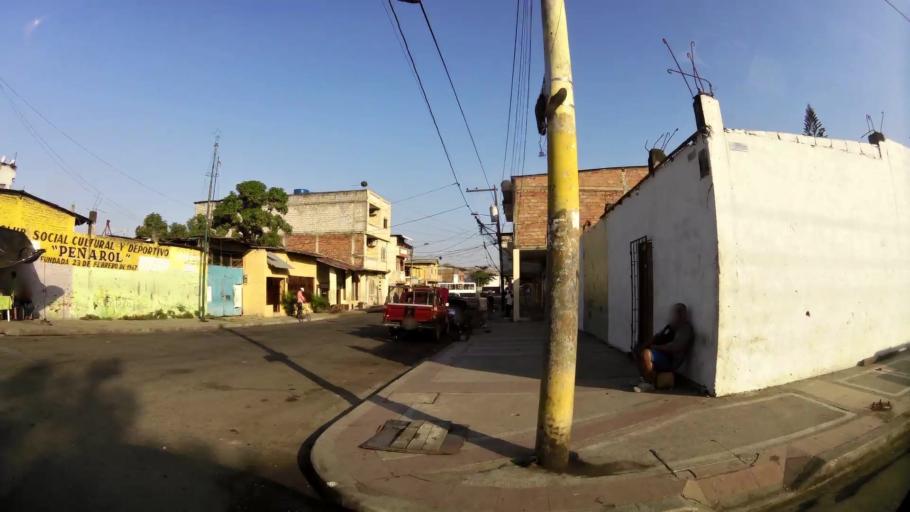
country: EC
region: Guayas
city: Eloy Alfaro
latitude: -2.1754
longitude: -79.8533
